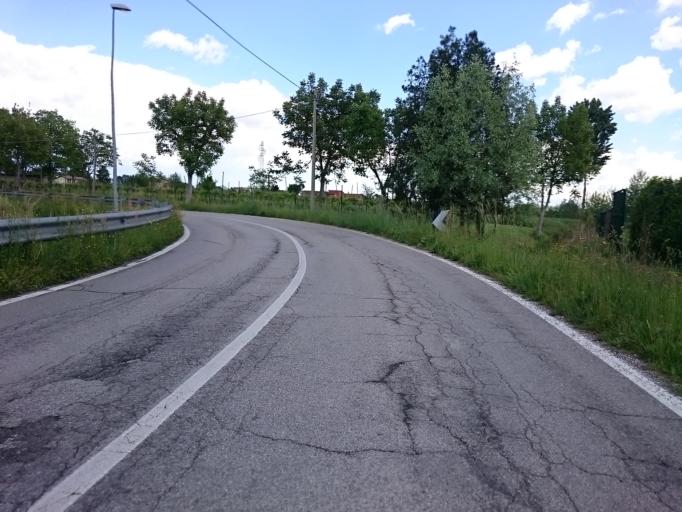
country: IT
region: Veneto
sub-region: Provincia di Padova
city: Terradura
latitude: 45.3423
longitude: 11.8115
